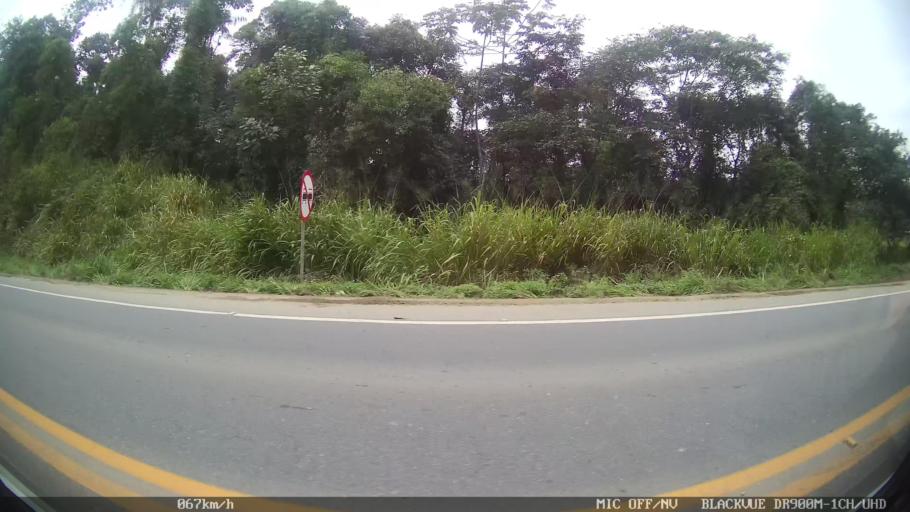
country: BR
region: Santa Catarina
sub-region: Joinville
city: Joinville
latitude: -26.2597
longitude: -48.9108
